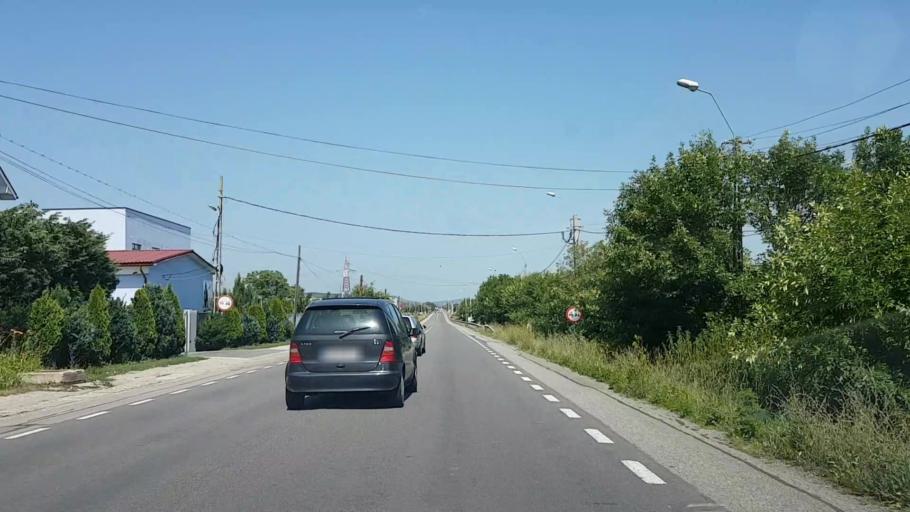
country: RO
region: Cluj
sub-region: Comuna Cusdrioara
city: Cusdrioara
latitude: 47.1732
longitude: 23.9320
